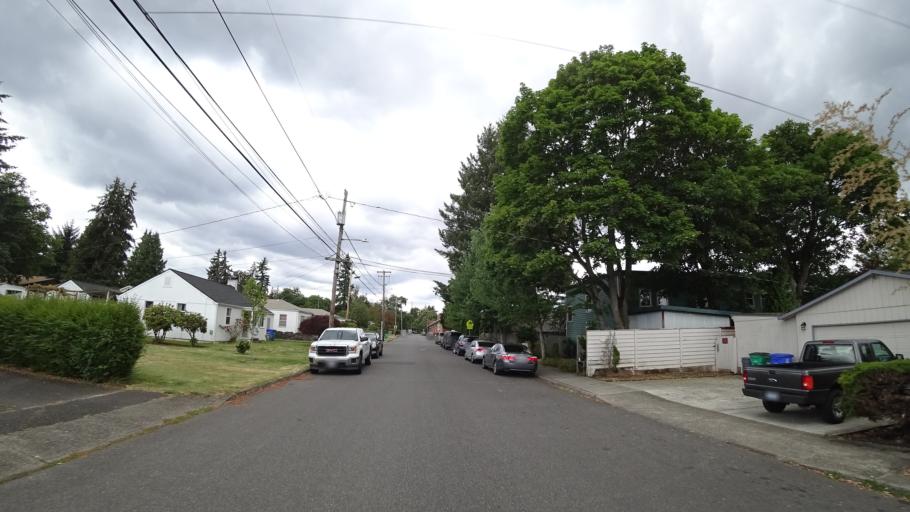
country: US
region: Oregon
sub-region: Multnomah County
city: Portland
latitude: 45.5615
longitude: -122.6175
